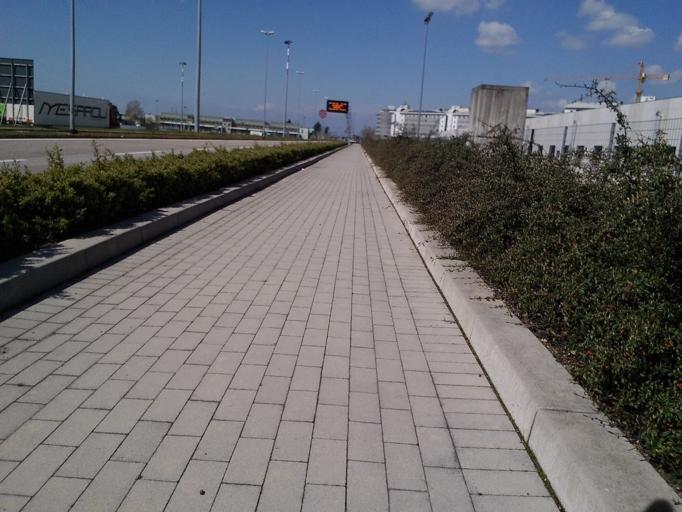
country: IT
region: Veneto
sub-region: Provincia di Verona
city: Dossobuono
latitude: 45.4113
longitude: 10.9273
